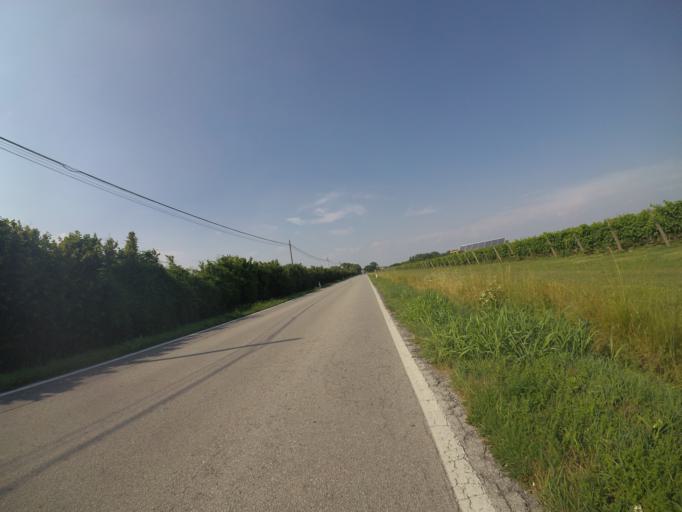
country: IT
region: Friuli Venezia Giulia
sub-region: Provincia di Udine
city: Camino al Tagliamento
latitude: 45.9360
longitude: 12.9602
